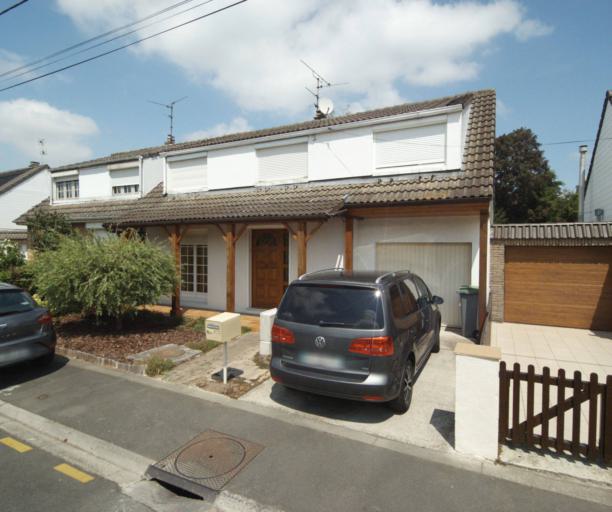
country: FR
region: Nord-Pas-de-Calais
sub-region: Departement du Nord
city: Armentieres
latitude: 50.6944
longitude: 2.8763
